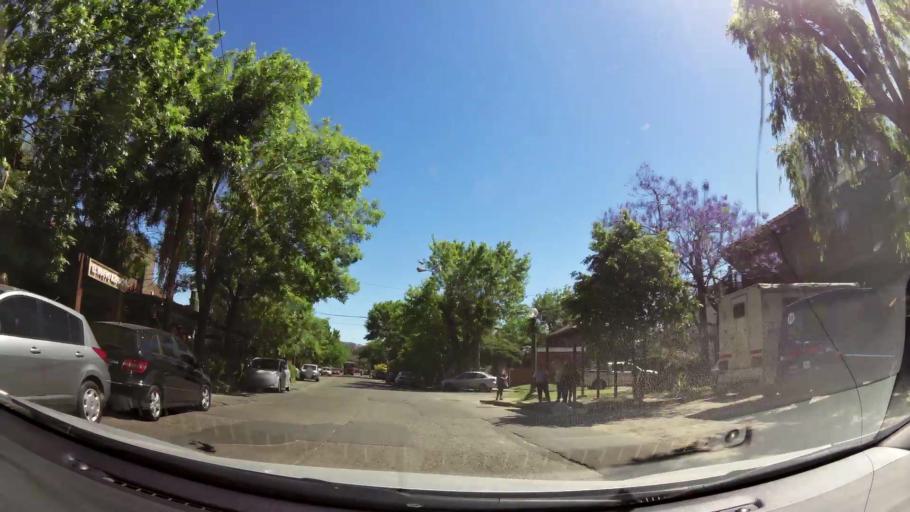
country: AR
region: Buenos Aires
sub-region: Partido de San Isidro
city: San Isidro
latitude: -34.4625
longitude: -58.5088
